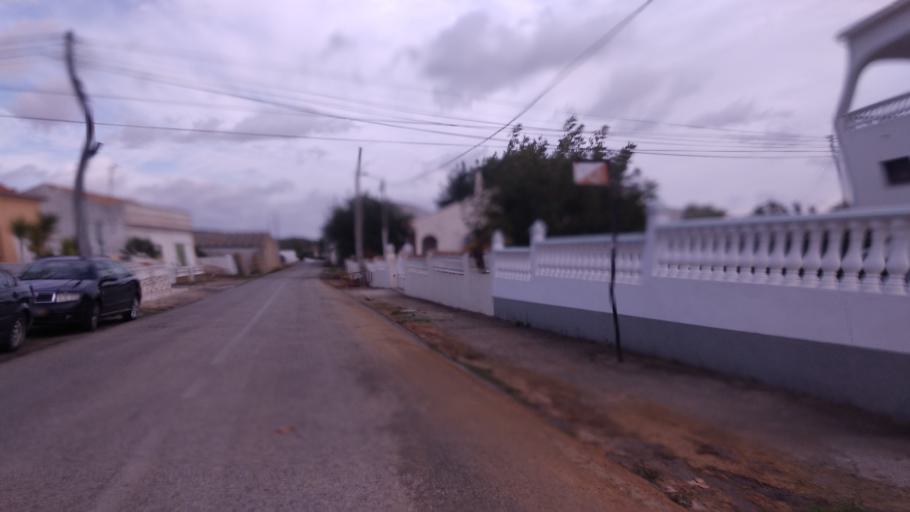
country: PT
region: Faro
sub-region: Sao Bras de Alportel
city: Sao Bras de Alportel
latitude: 37.1682
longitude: -7.9058
